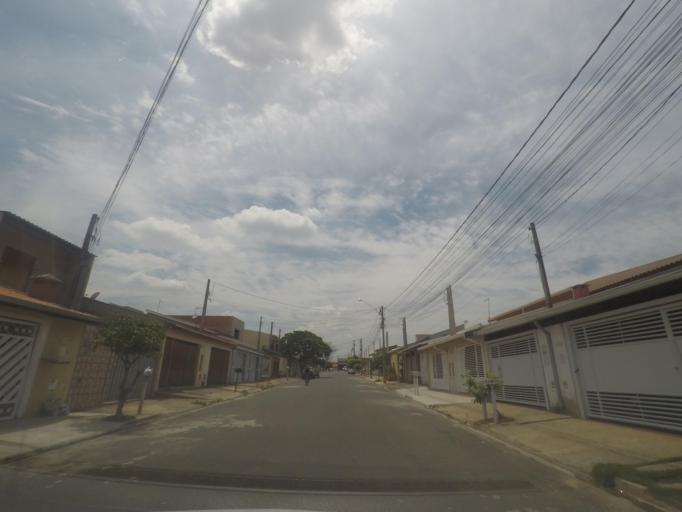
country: BR
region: Sao Paulo
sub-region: Sumare
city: Sumare
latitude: -22.7990
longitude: -47.2708
